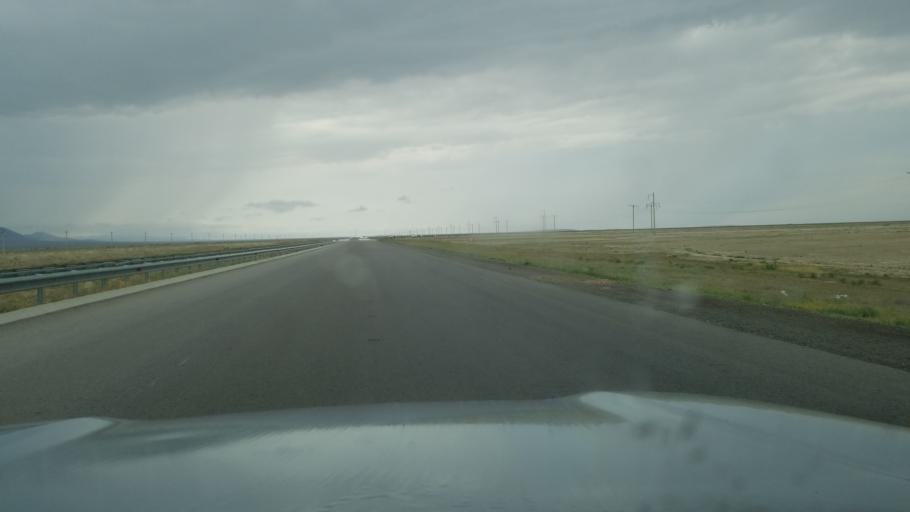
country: TM
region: Balkan
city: Serdar
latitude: 39.0410
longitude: 56.1543
